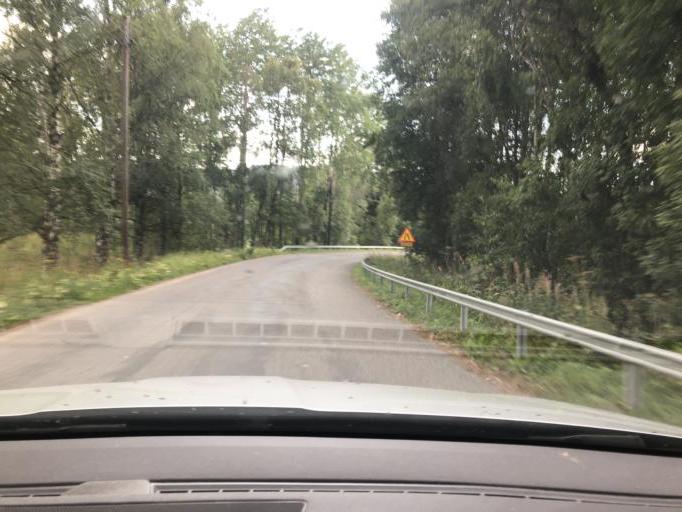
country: SE
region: Vaesternorrland
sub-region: Solleftea Kommun
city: Solleftea
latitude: 63.2455
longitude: 17.2013
